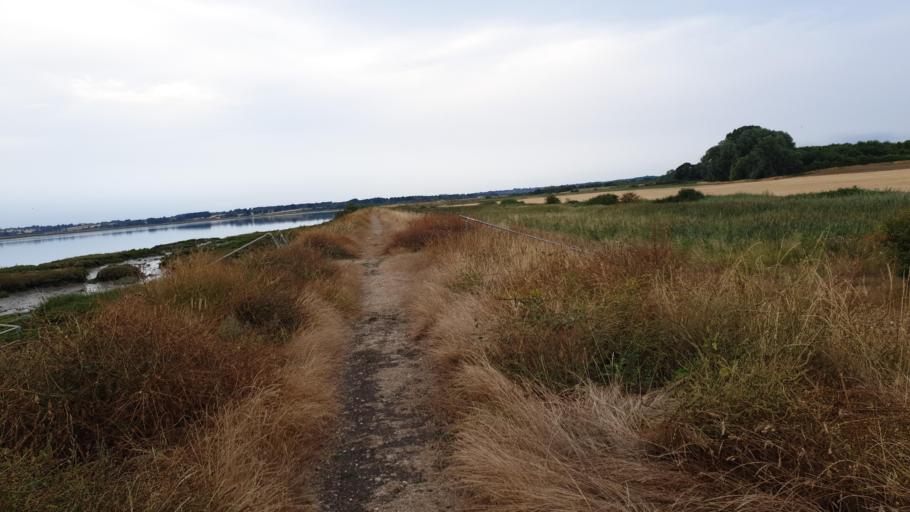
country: GB
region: England
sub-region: Essex
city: Brightlingsea
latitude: 51.8188
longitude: 0.9930
